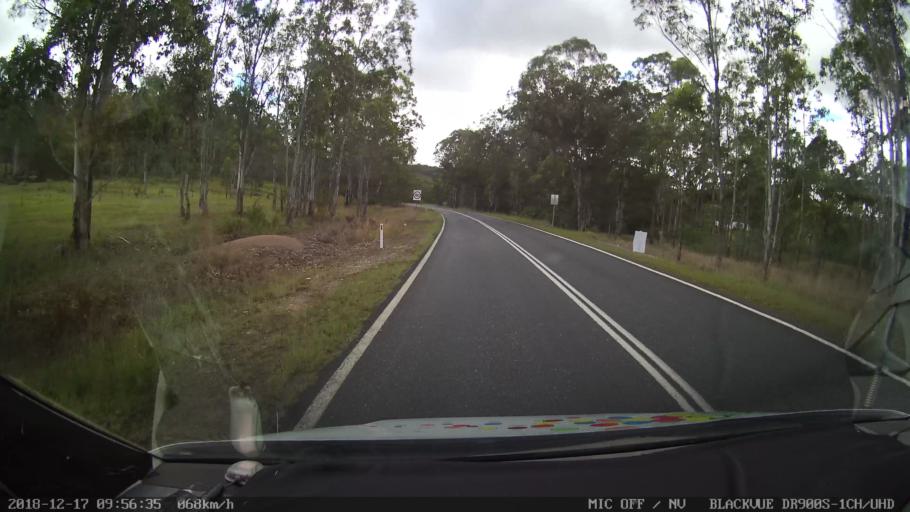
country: AU
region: New South Wales
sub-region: Tenterfield Municipality
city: Carrolls Creek
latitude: -28.9309
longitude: 152.3890
